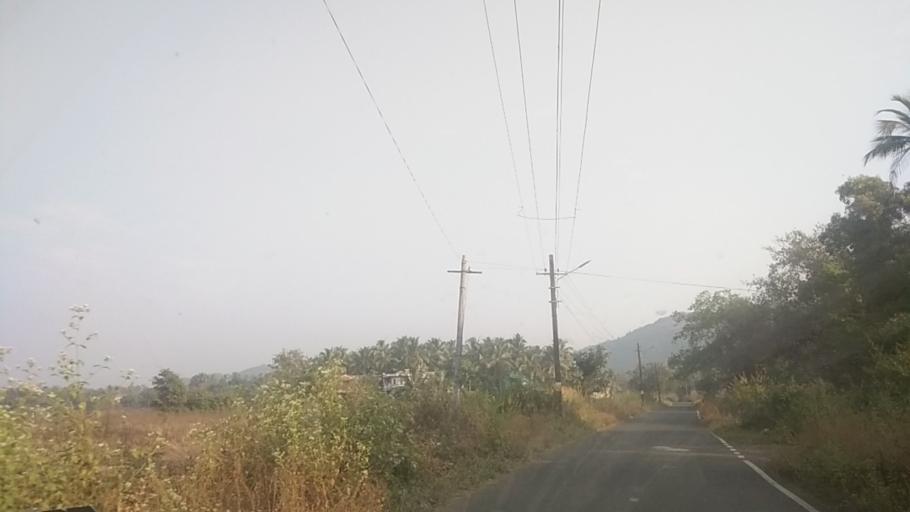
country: IN
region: Goa
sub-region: South Goa
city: Chinchinim
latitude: 15.2276
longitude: 73.9915
